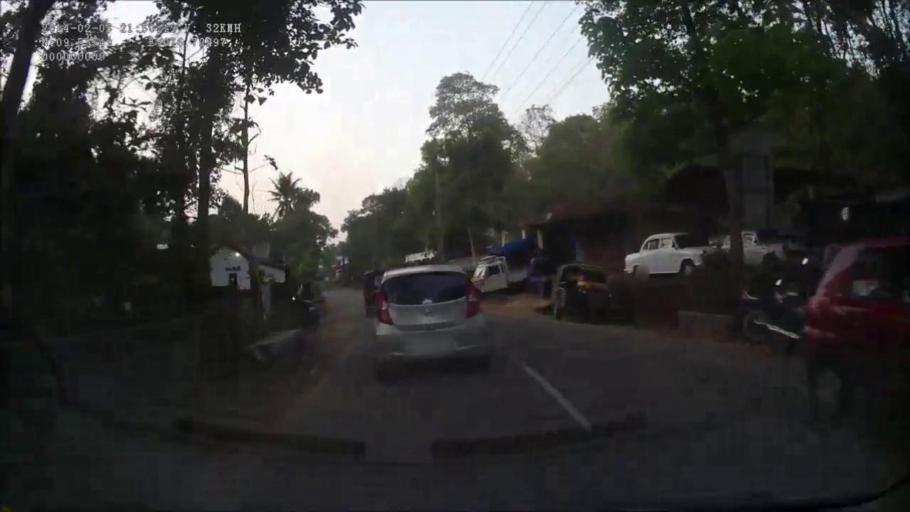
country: IN
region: Kerala
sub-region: Kottayam
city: Erattupetta
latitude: 9.5353
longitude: 76.7232
